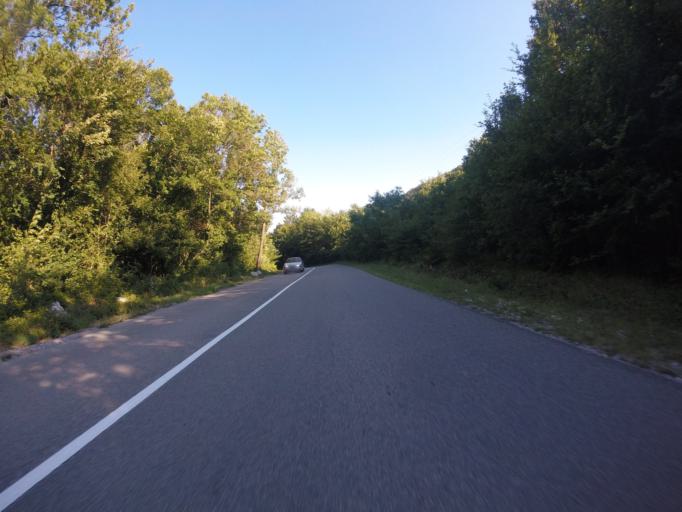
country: HR
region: Primorsko-Goranska
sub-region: Grad Crikvenica
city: Jadranovo
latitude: 45.2573
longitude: 14.6129
